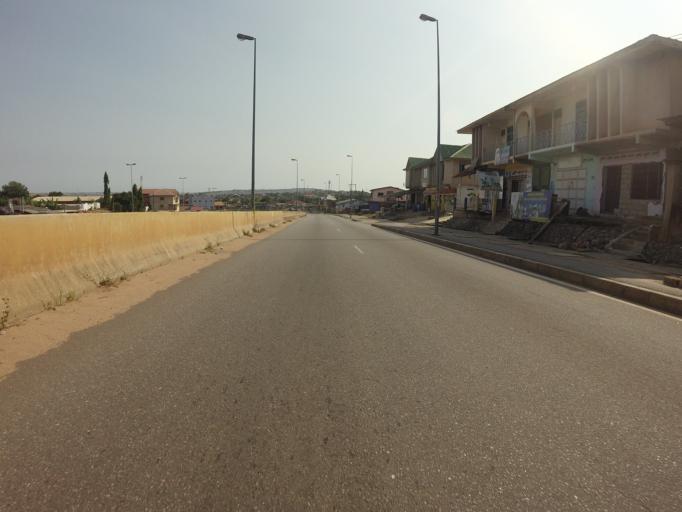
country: GH
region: Greater Accra
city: Gbawe
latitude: 5.6116
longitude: -0.2971
